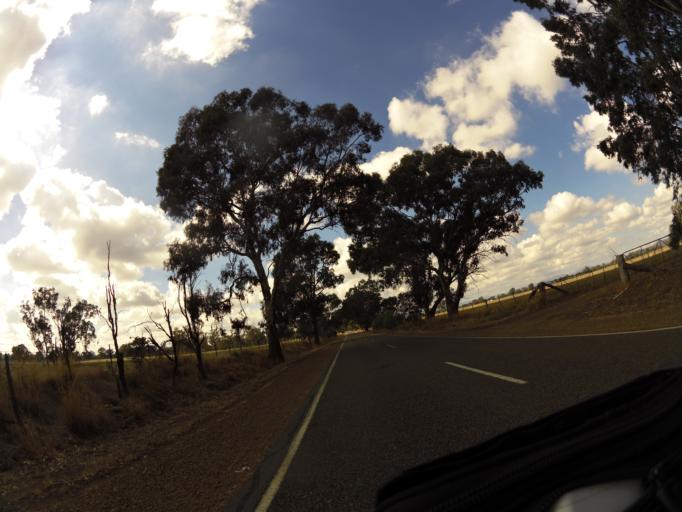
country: AU
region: Victoria
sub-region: Benalla
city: Benalla
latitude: -36.6148
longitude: 146.0264
